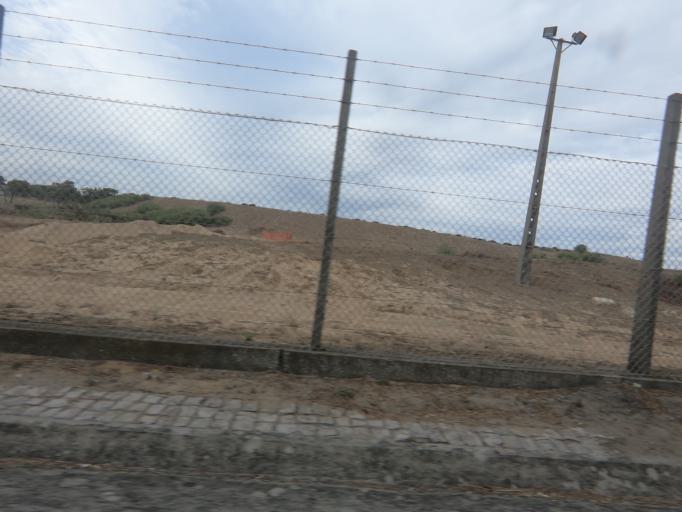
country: PT
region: Setubal
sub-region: Almada
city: Charneca
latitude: 38.6080
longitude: -9.2013
